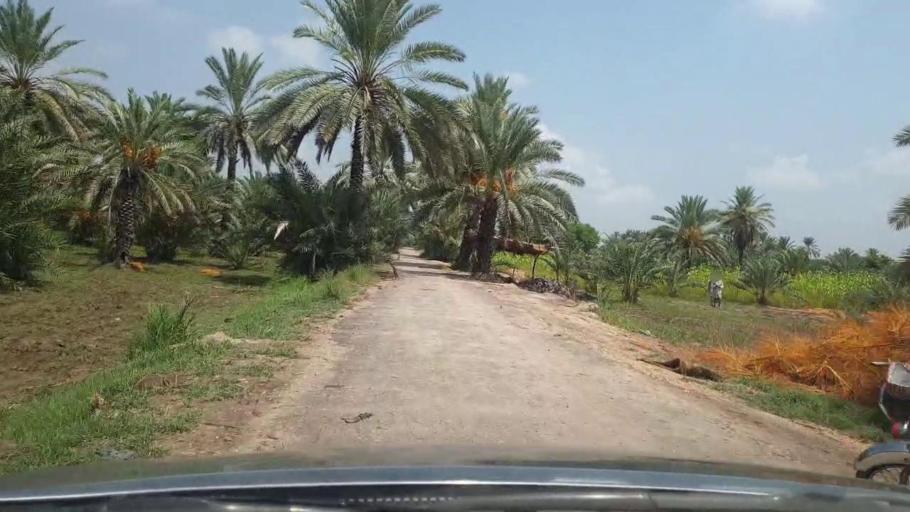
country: PK
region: Sindh
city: Pir jo Goth
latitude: 27.6212
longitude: 68.6658
